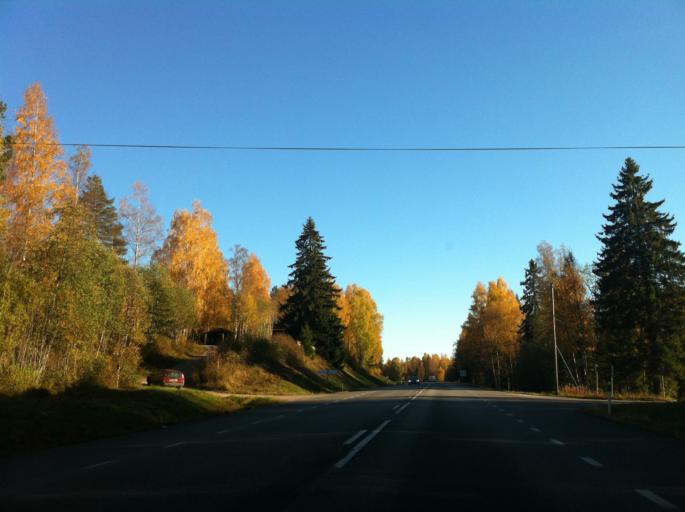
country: SE
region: Dalarna
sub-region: Rattviks Kommun
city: Raettvik
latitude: 60.9055
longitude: 15.0685
